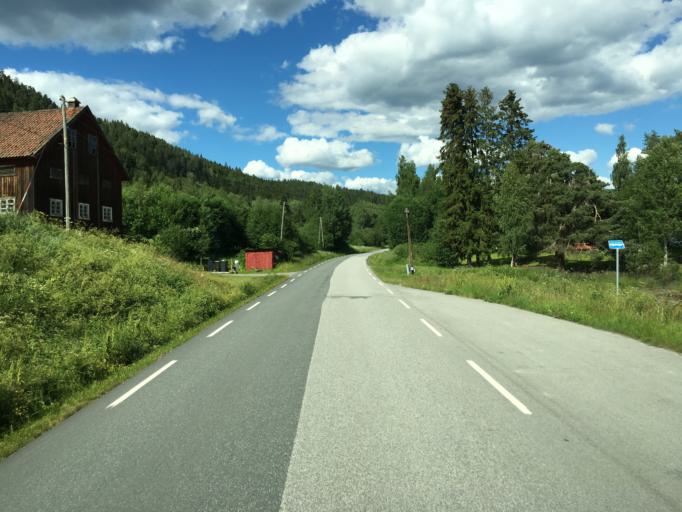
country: NO
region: Oppland
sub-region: Sondre Land
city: Hov
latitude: 60.6137
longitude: 10.3332
